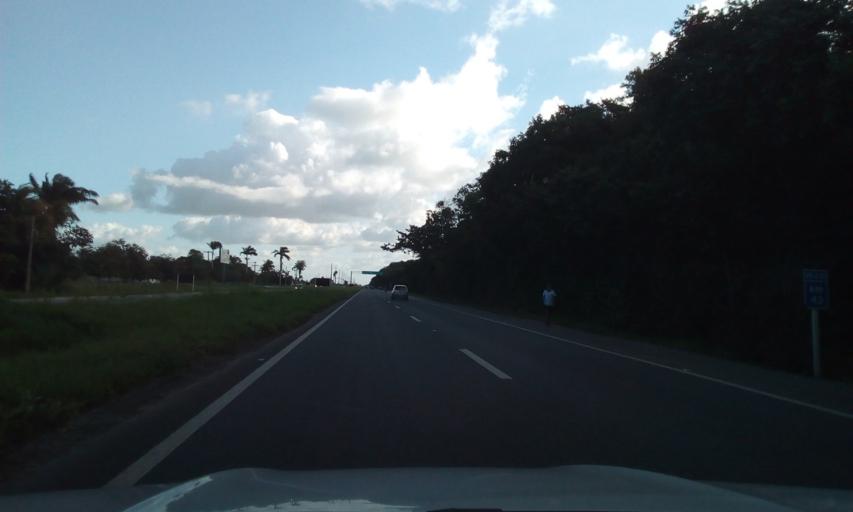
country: BR
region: Paraiba
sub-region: Santa Rita
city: Santa Rita
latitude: -7.1498
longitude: -35.0056
